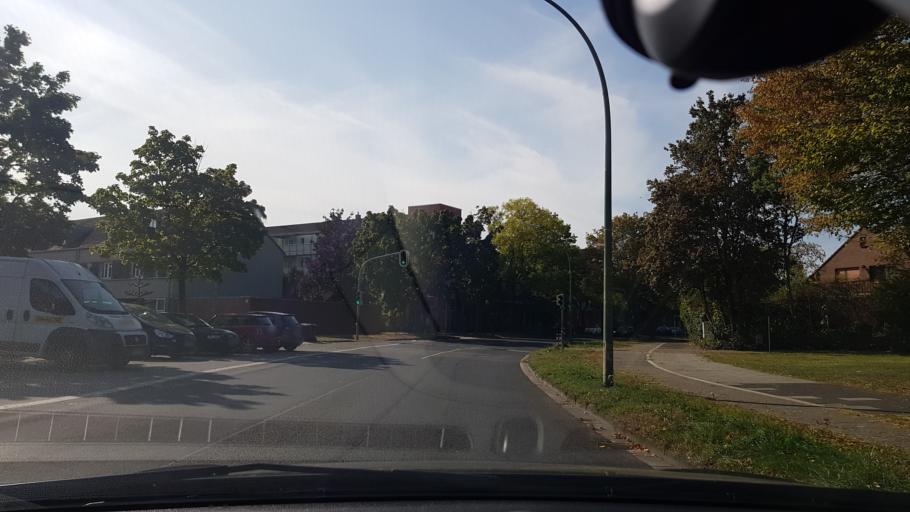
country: DE
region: North Rhine-Westphalia
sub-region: Regierungsbezirk Dusseldorf
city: Neuss
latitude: 51.1543
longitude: 6.7038
